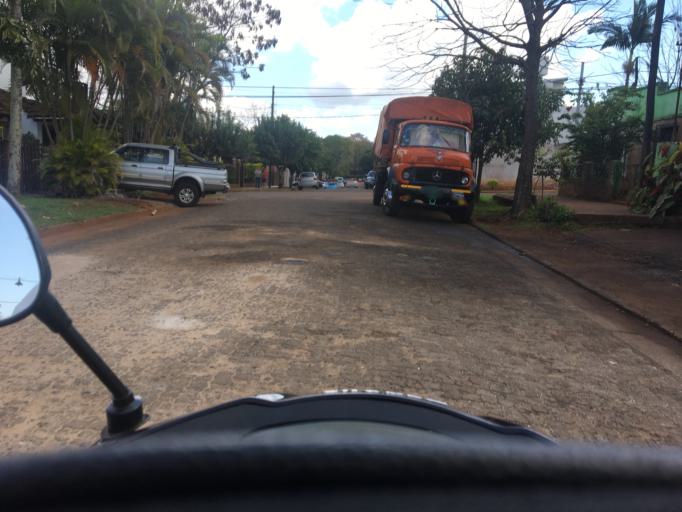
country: AR
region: Misiones
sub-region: Departamento de Capital
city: Posadas
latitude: -27.3960
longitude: -55.9033
